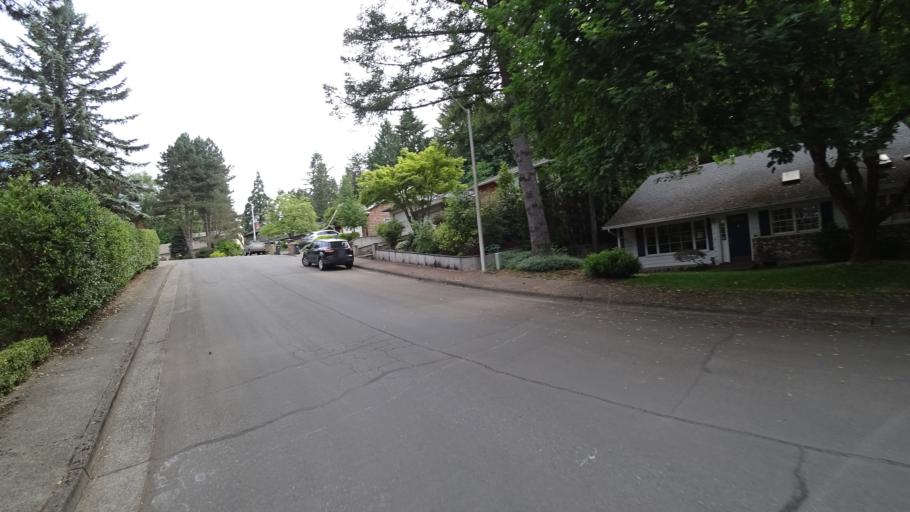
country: US
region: Oregon
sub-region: Clackamas County
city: Lake Oswego
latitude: 45.4310
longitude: -122.6761
